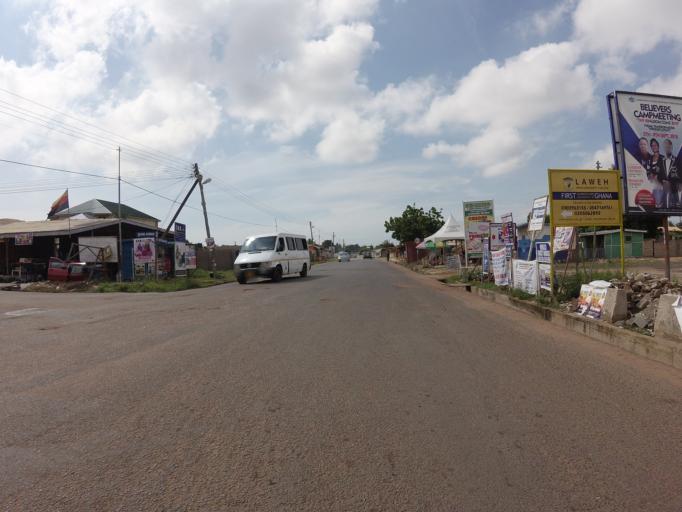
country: GH
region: Greater Accra
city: Nungua
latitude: 5.6123
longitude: -0.0908
